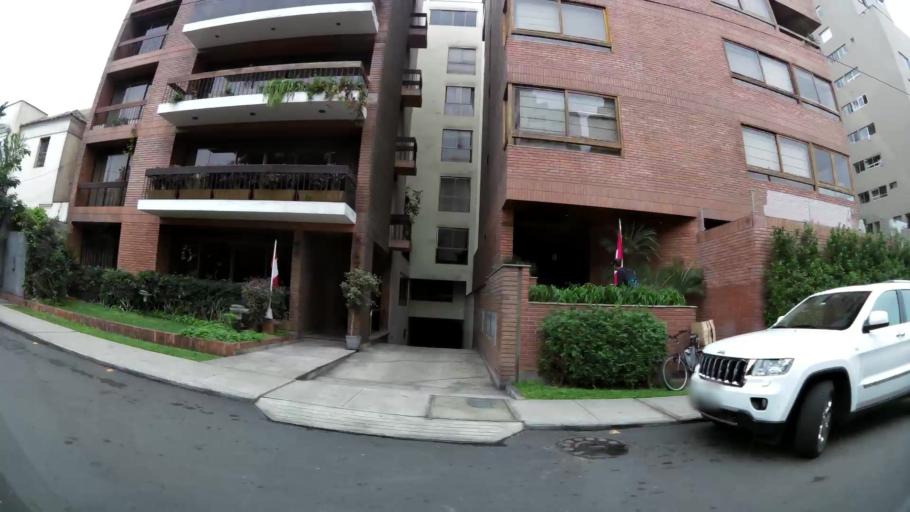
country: PE
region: Lima
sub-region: Lima
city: San Isidro
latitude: -12.0983
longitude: -77.0468
